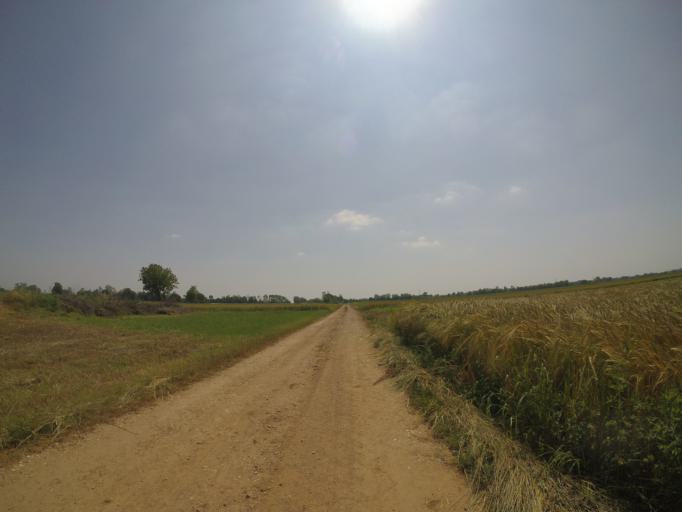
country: IT
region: Friuli Venezia Giulia
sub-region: Provincia di Udine
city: Bertiolo
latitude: 45.9716
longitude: 13.0756
